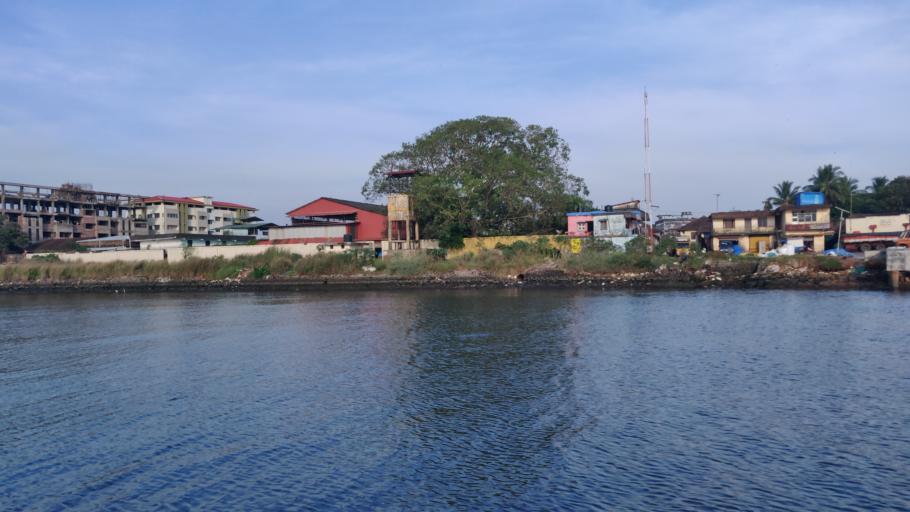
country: IN
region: Karnataka
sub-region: Dakshina Kannada
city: Mangalore
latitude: 12.8654
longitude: 74.8304
